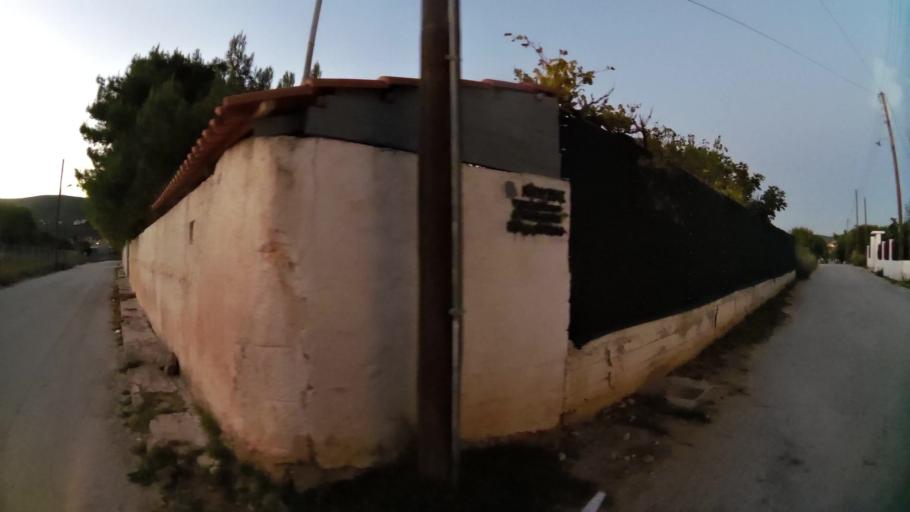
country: GR
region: Attica
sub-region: Nomarchia Anatolikis Attikis
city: Agia Marina
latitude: 37.8232
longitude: 23.8559
